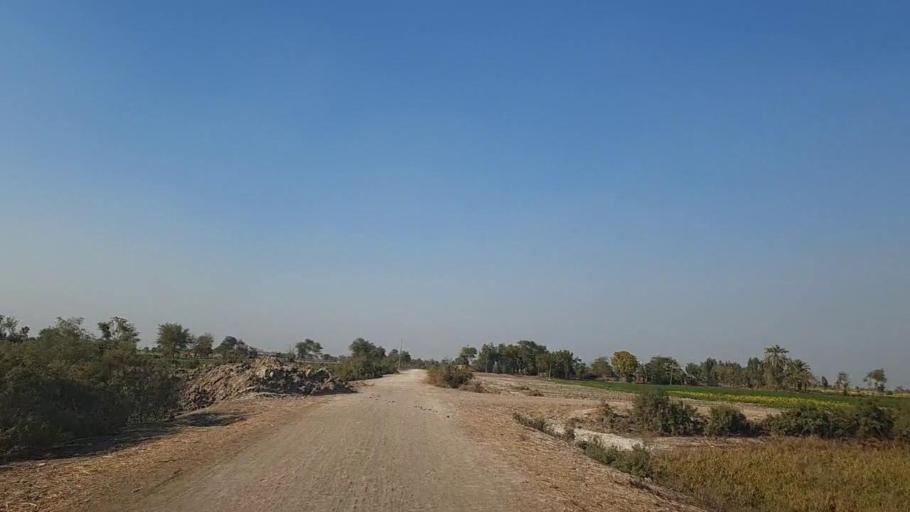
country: PK
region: Sindh
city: Daur
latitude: 26.3249
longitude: 68.1778
